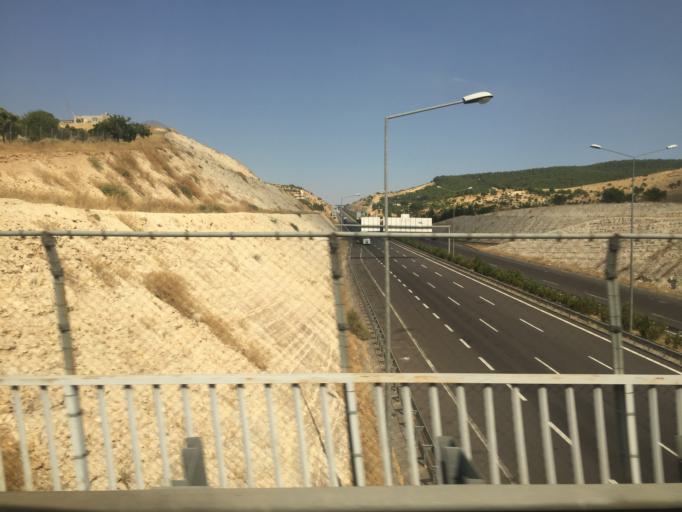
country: TR
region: Sanliurfa
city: Akziyaret
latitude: 37.2695
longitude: 38.8015
